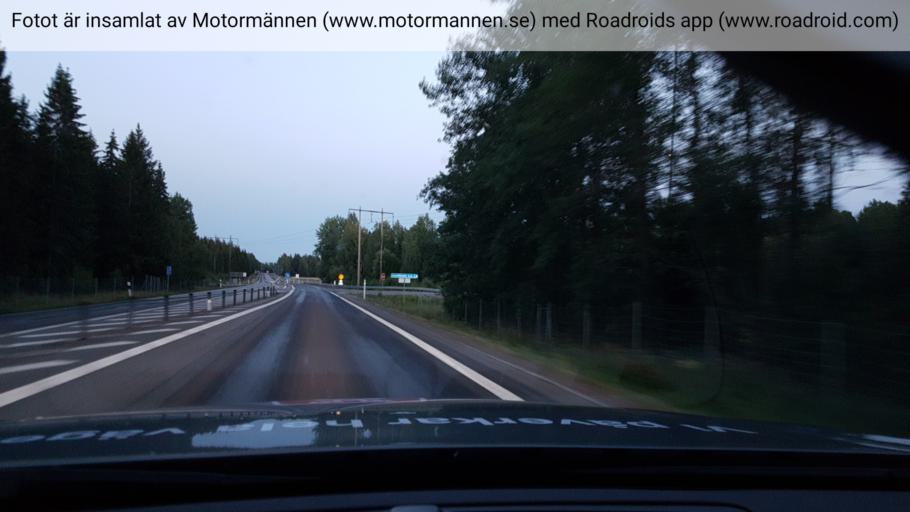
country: SE
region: Vaestmanland
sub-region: Vasteras
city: Skultuna
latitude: 59.6493
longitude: 16.3906
